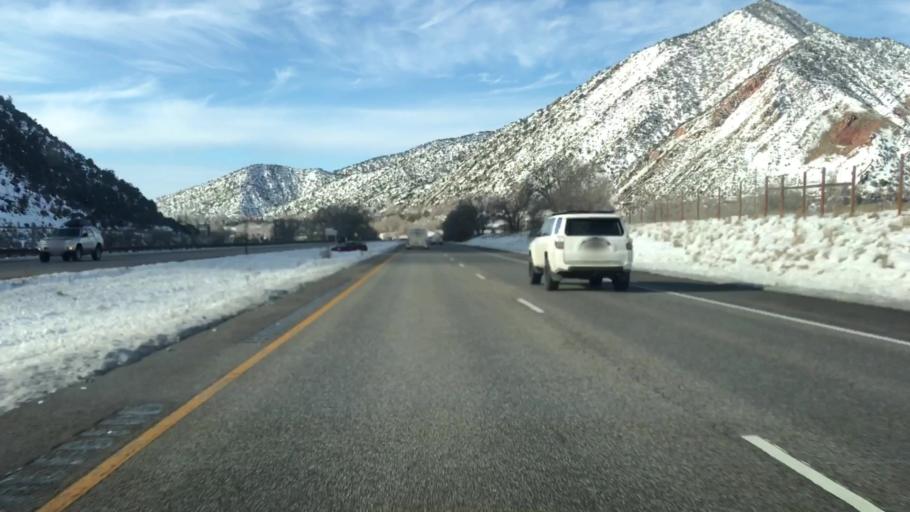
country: US
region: Colorado
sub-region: Garfield County
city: New Castle
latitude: 39.5703
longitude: -107.5336
